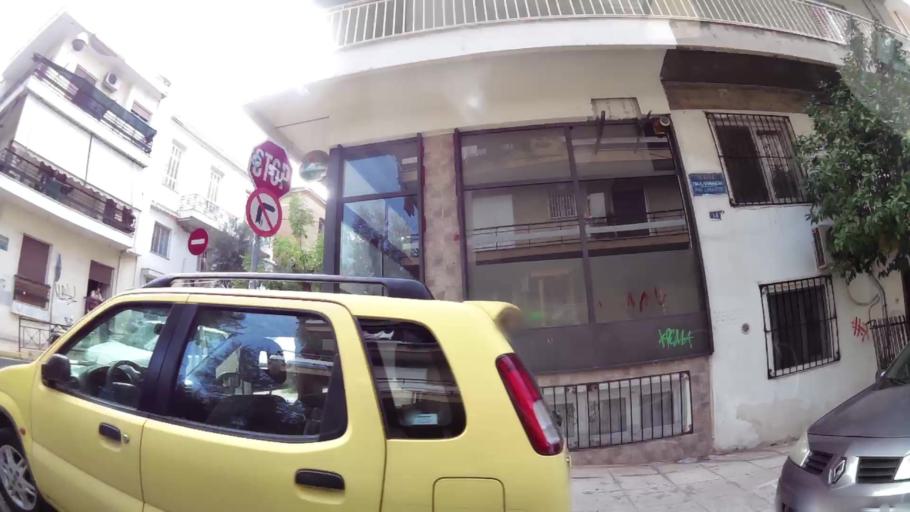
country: GR
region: Attica
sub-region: Nomarchia Athinas
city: Athens
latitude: 37.9708
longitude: 23.7129
